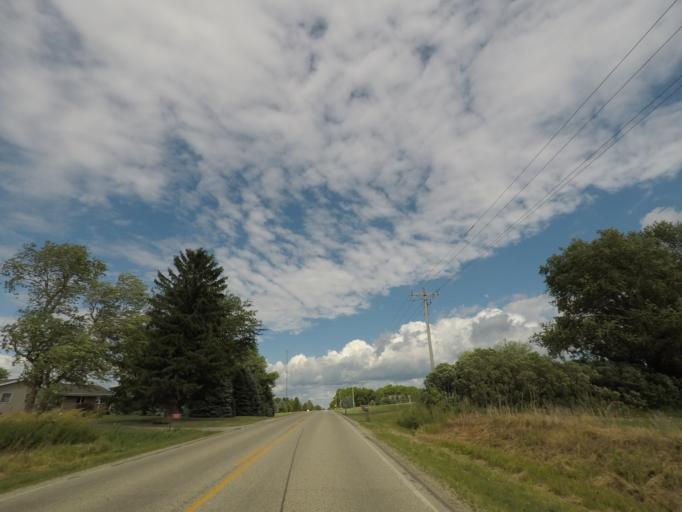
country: US
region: Wisconsin
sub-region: Rock County
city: Janesville
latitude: 42.7012
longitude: -89.1119
